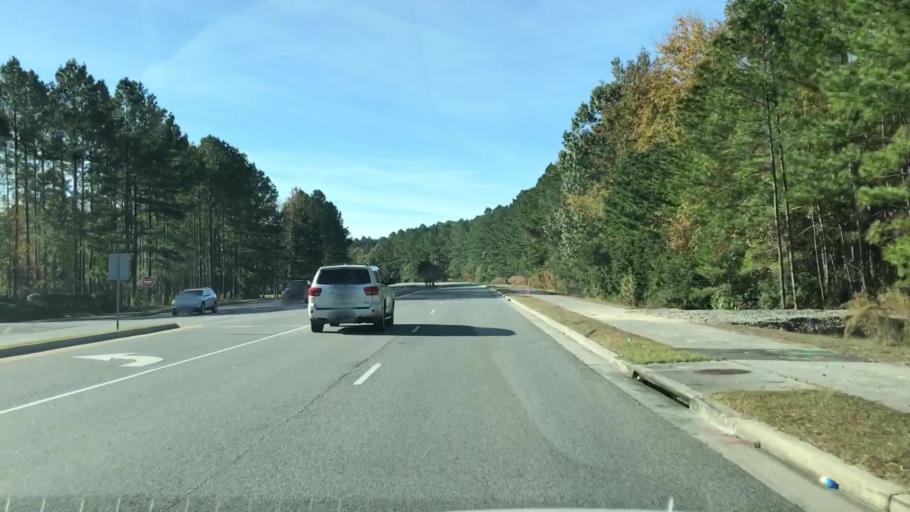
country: US
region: South Carolina
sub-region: Beaufort County
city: Bluffton
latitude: 32.2811
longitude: -80.9120
